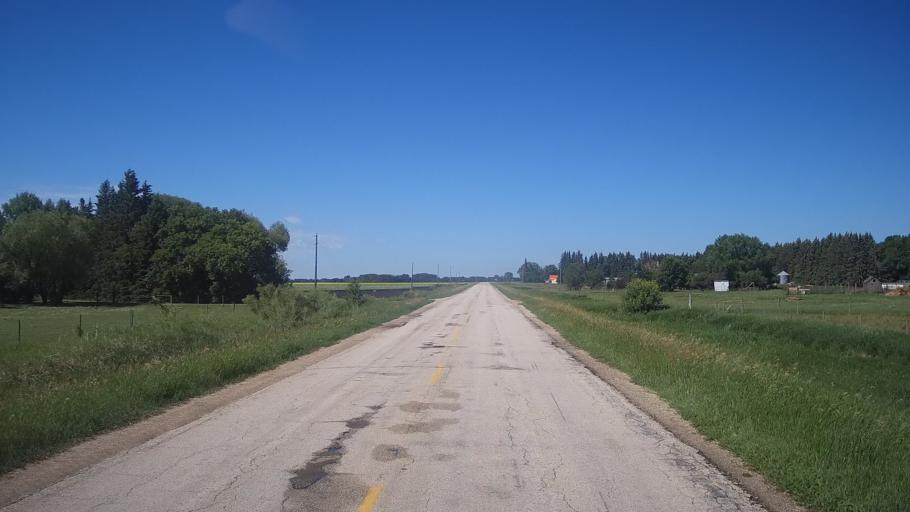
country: CA
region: Manitoba
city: Portage la Prairie
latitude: 50.0376
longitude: -98.0753
